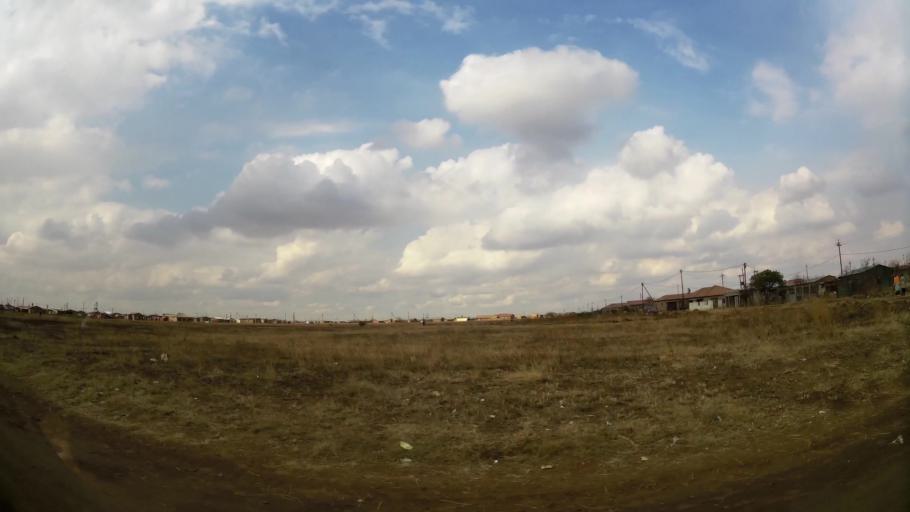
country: ZA
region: Orange Free State
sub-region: Fezile Dabi District Municipality
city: Sasolburg
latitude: -26.8559
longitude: 27.8981
